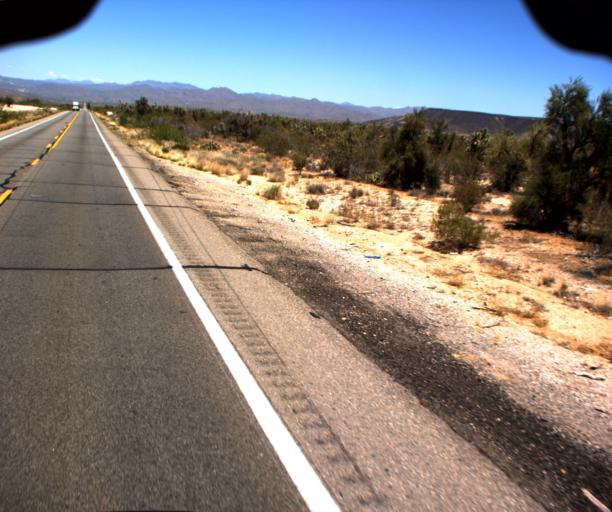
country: US
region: Arizona
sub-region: Yavapai County
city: Bagdad
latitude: 34.2927
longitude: -113.1122
